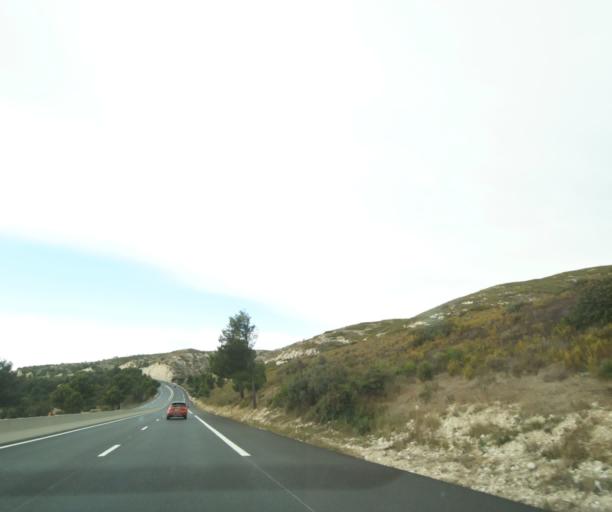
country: FR
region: Provence-Alpes-Cote d'Azur
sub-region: Departement des Bouches-du-Rhone
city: Carry-le-Rouet
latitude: 43.3416
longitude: 5.1319
